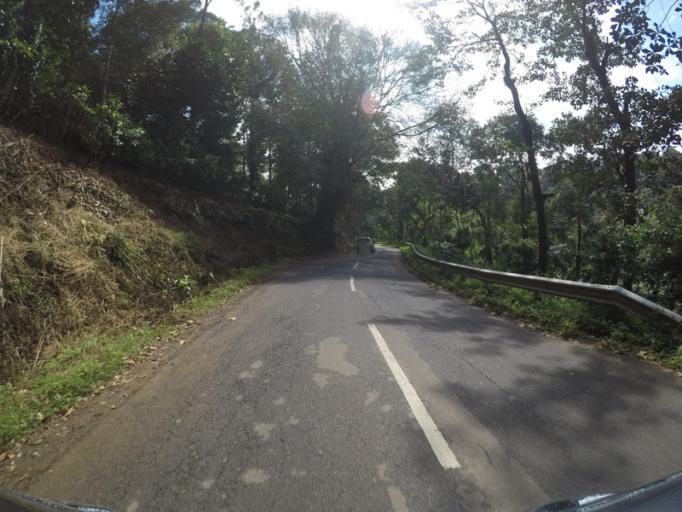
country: IN
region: Karnataka
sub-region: Kodagu
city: Suntikoppa
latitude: 12.4769
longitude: 75.7880
